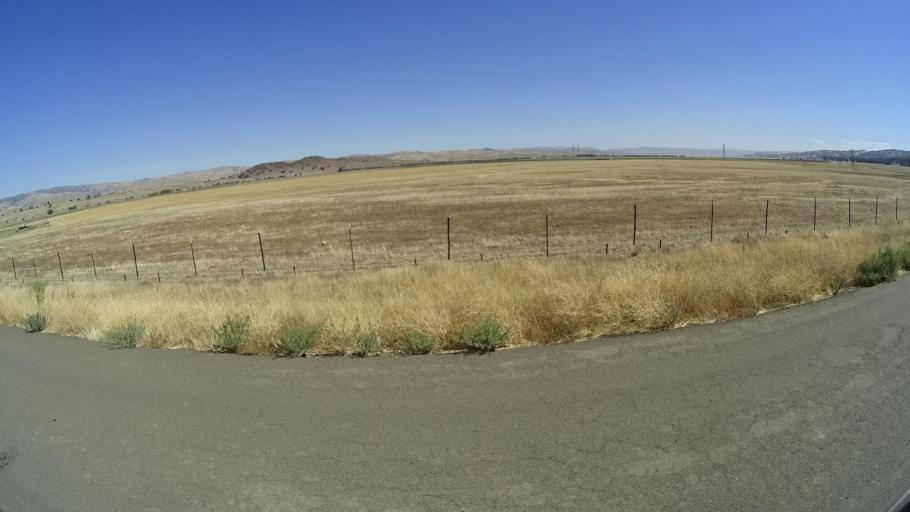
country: US
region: California
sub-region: San Luis Obispo County
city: Shandon
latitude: 35.8268
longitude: -120.3863
